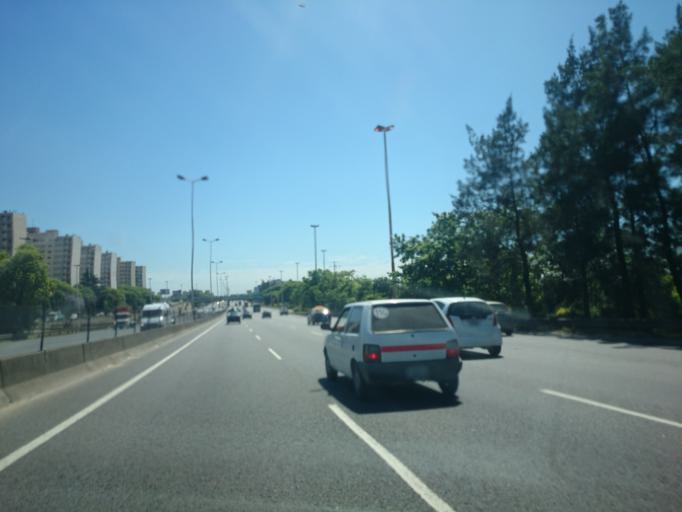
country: AR
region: Buenos Aires F.D.
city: Villa Lugano
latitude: -34.7091
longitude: -58.5037
